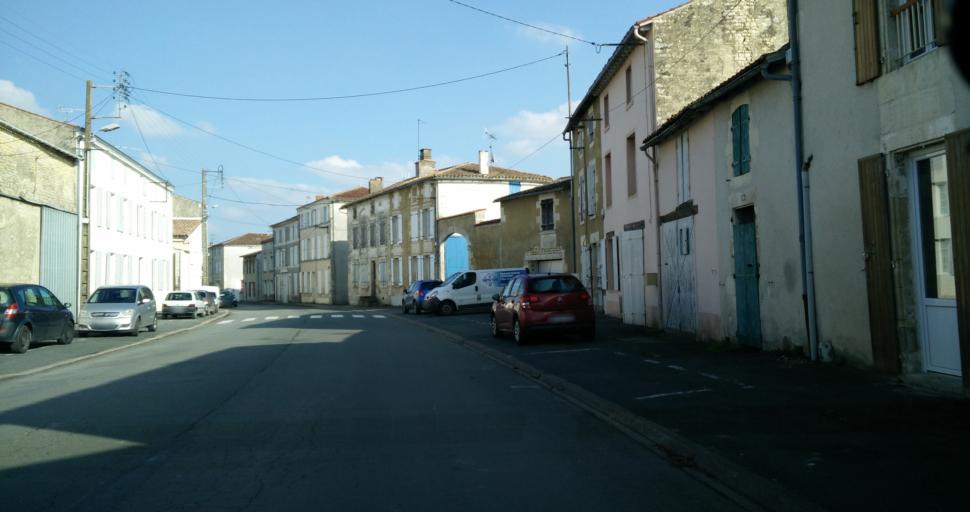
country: FR
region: Poitou-Charentes
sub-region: Departement des Deux-Sevres
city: Mauze-sur-le-Mignon
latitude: 46.1917
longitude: -0.6769
